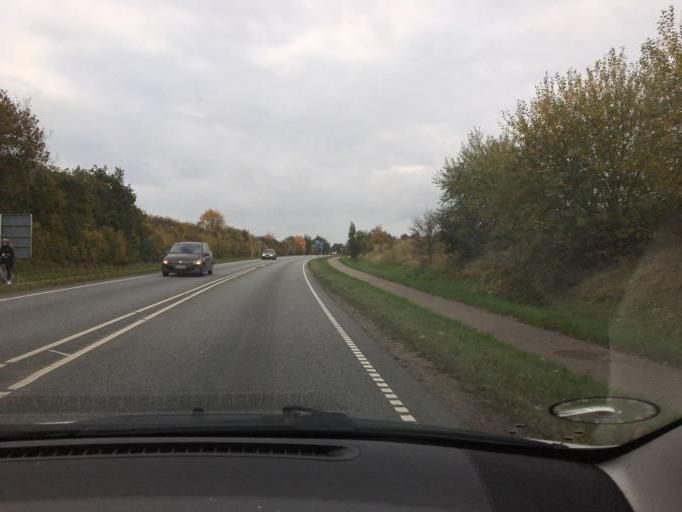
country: DK
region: South Denmark
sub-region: Fredericia Kommune
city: Fredericia
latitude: 55.6067
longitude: 9.7570
